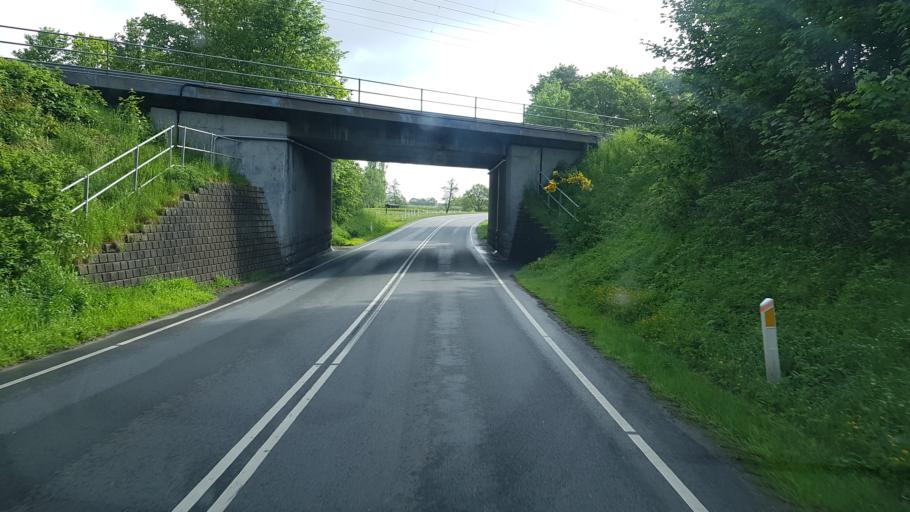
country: DK
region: South Denmark
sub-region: Vejen Kommune
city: Vejen
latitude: 55.4667
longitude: 9.1770
